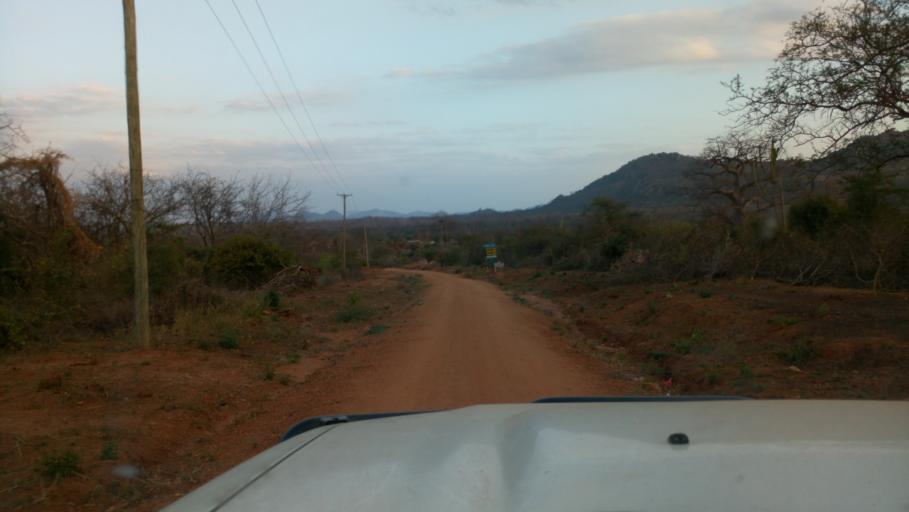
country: KE
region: Kitui
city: Kitui
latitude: -1.6758
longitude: 38.2214
